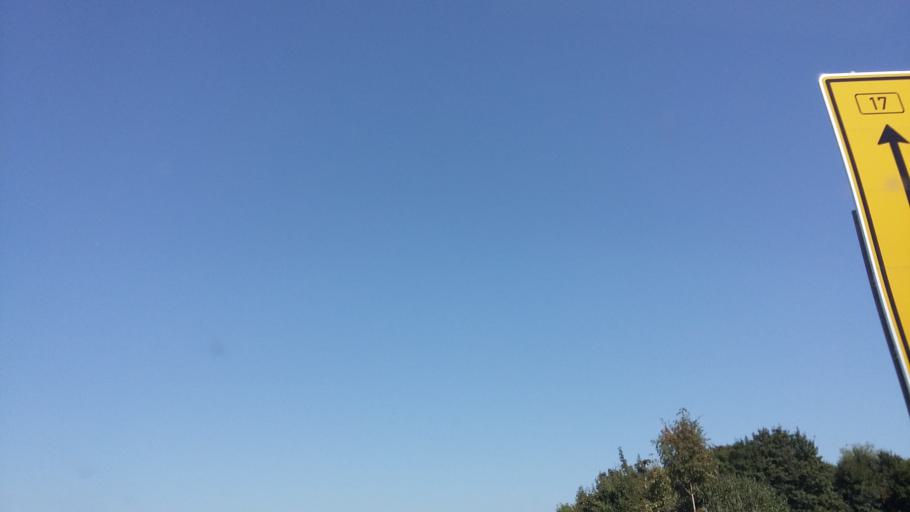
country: DE
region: Bavaria
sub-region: Swabia
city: Graben
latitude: 48.1903
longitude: 10.8487
